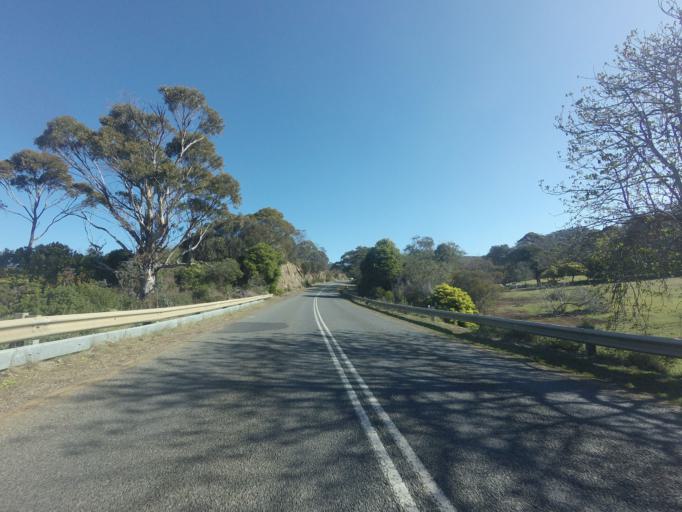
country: AU
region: Tasmania
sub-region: Sorell
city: Sorell
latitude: -42.2281
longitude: 148.0241
